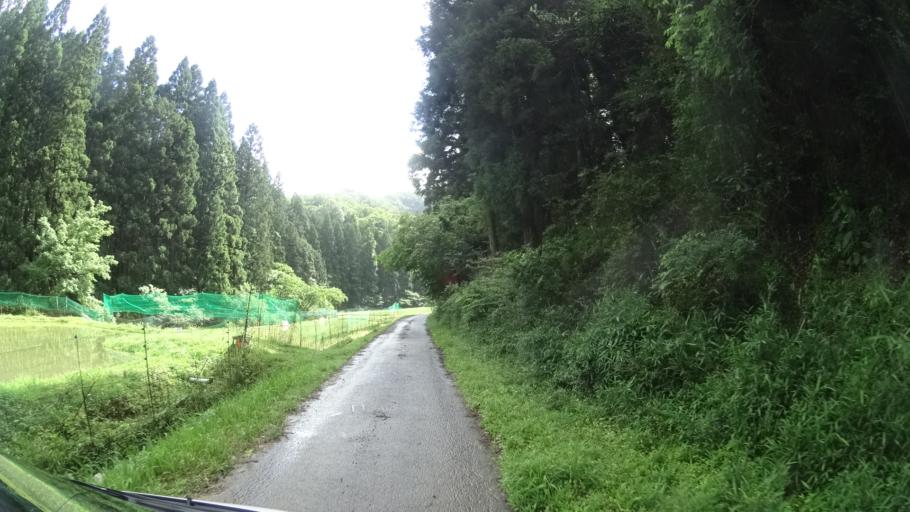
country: JP
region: Kyoto
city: Maizuru
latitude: 35.3909
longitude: 135.2753
